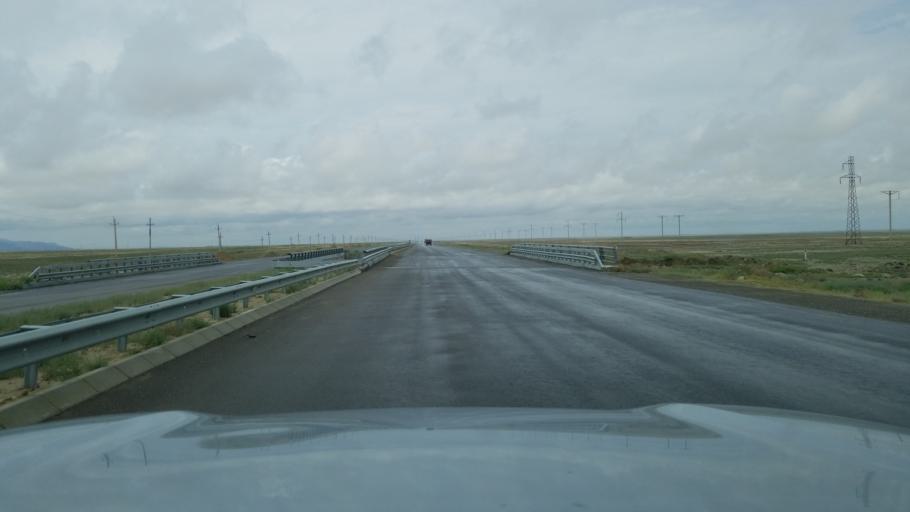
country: TM
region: Balkan
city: Gazanjyk
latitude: 39.1874
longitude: 55.7922
